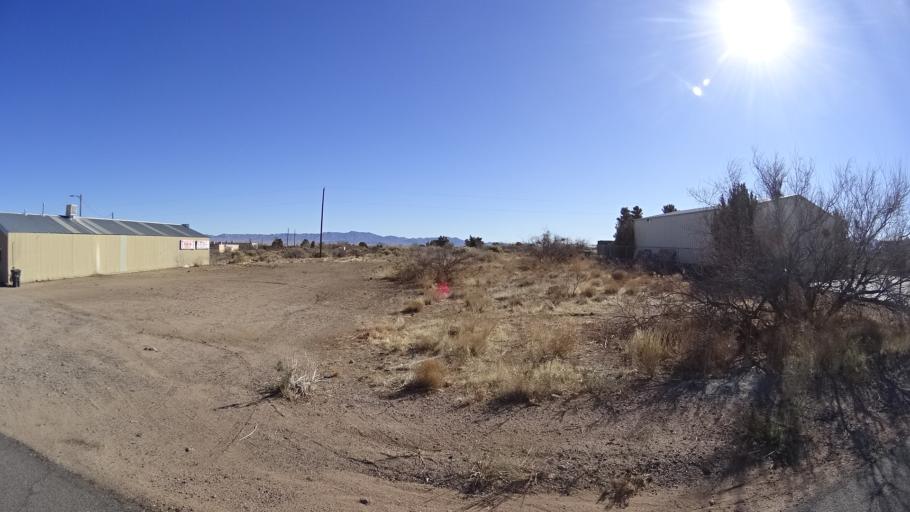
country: US
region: Arizona
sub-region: Mohave County
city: New Kingman-Butler
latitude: 35.2571
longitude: -114.0396
